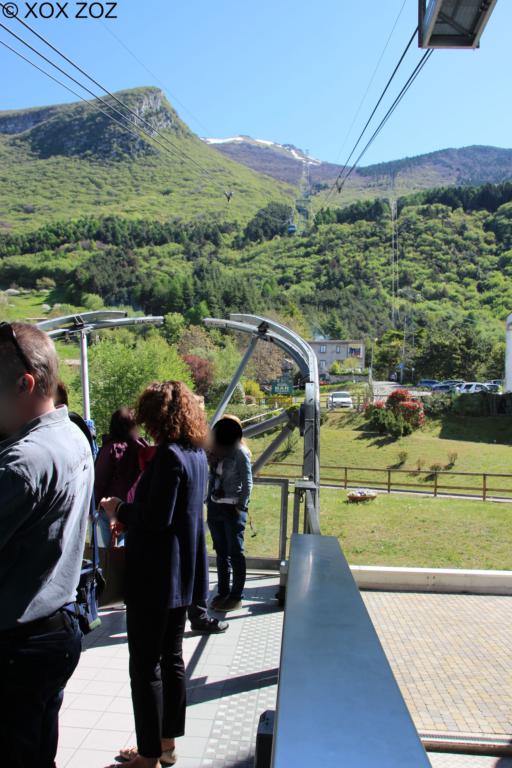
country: IT
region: Veneto
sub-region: Provincia di Verona
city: Malcesine
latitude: 45.7688
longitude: 10.8318
